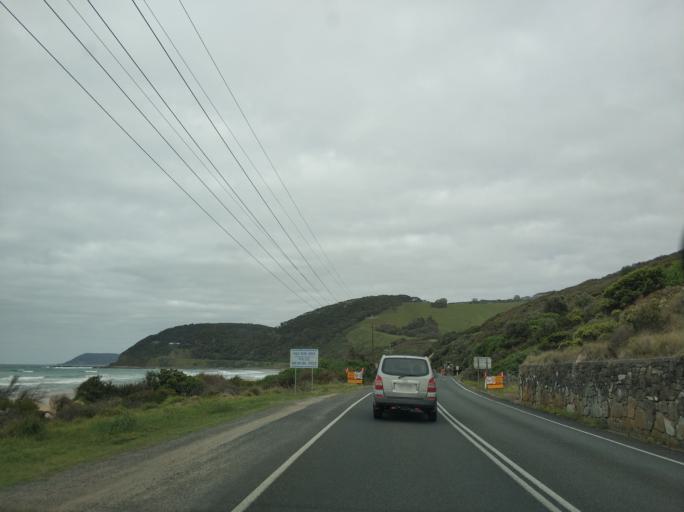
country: AU
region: Victoria
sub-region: Surf Coast
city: Anglesea
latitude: -38.4730
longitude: 144.0418
